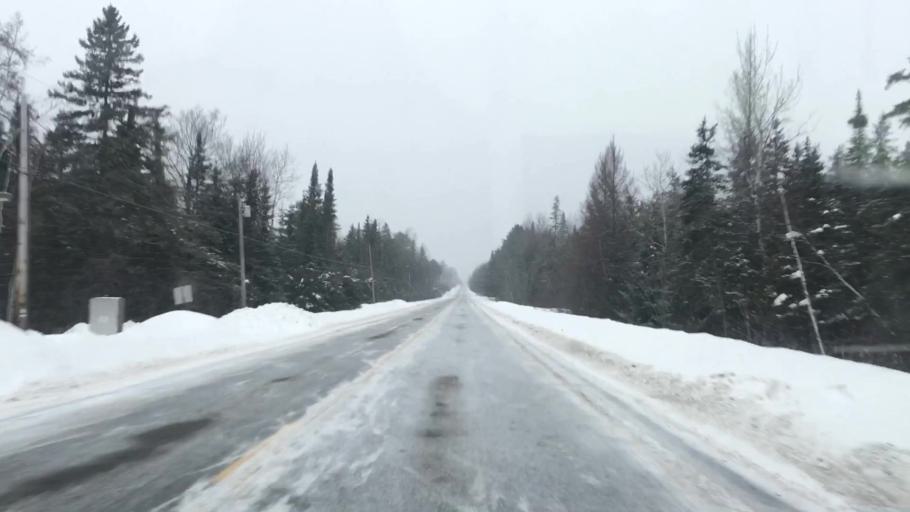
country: US
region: Maine
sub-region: Penobscot County
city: Medway
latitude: 45.5265
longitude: -68.3580
